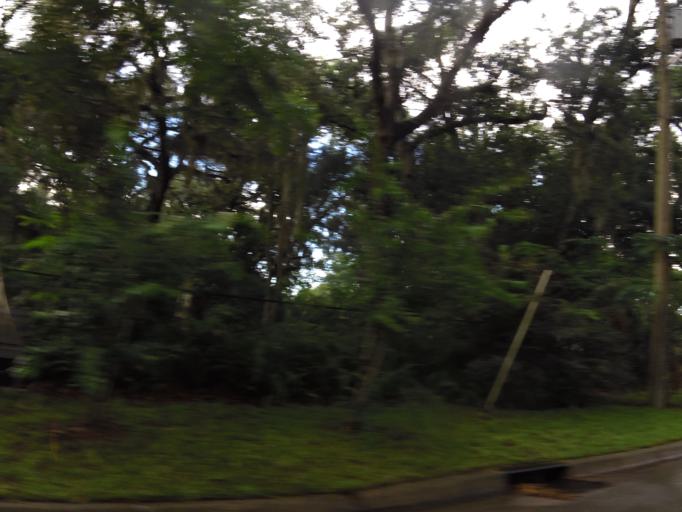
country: US
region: Florida
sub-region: Duval County
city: Jacksonville
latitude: 30.3075
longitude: -81.6309
